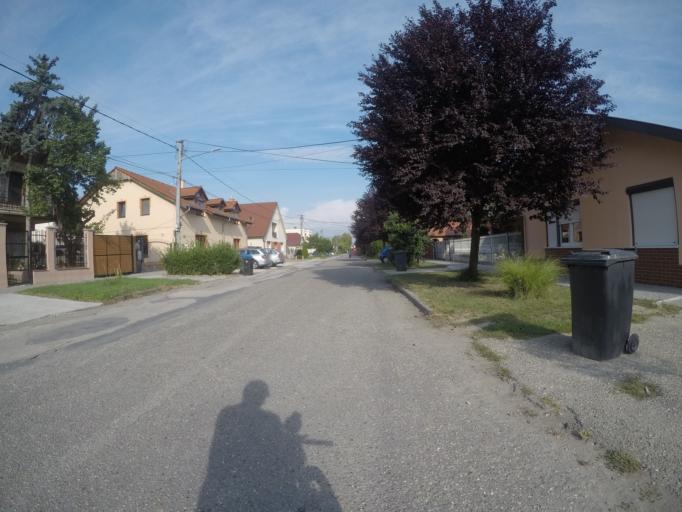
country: SK
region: Trnavsky
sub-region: Okres Dunajska Streda
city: Velky Meder
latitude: 47.8552
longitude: 17.7626
